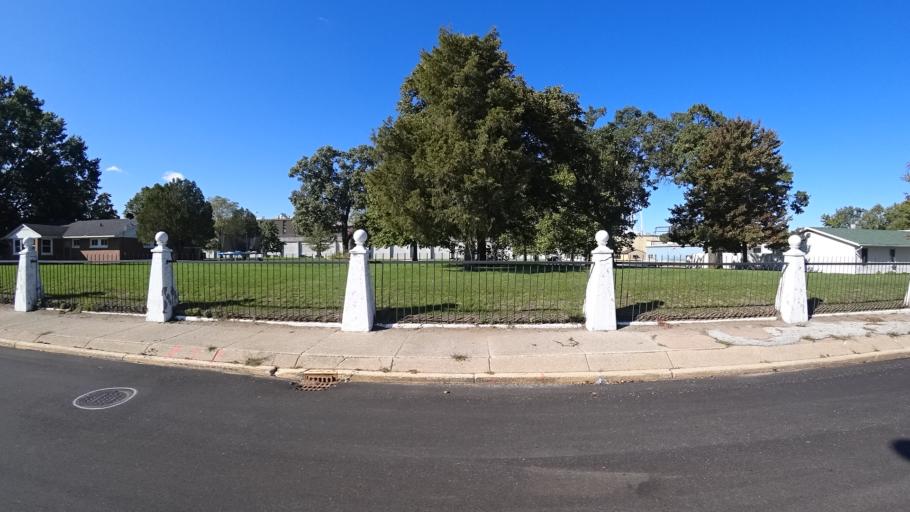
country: US
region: Indiana
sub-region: LaPorte County
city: Michigan City
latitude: 41.7046
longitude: -86.9140
